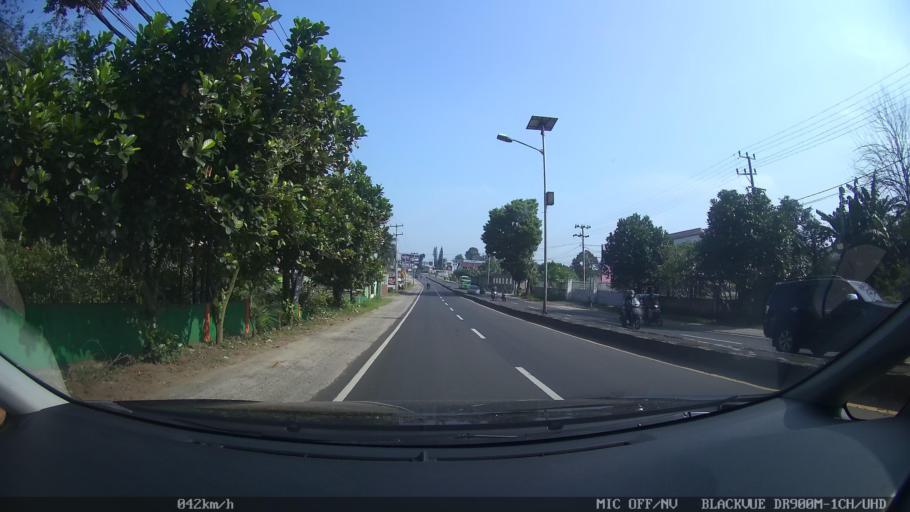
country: ID
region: Lampung
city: Natar
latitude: -5.3424
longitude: 105.2141
